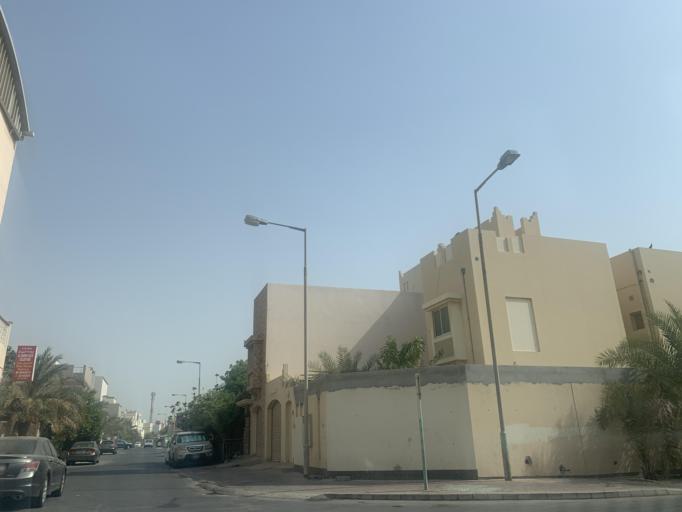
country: BH
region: Manama
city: Jidd Hafs
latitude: 26.2109
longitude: 50.4719
